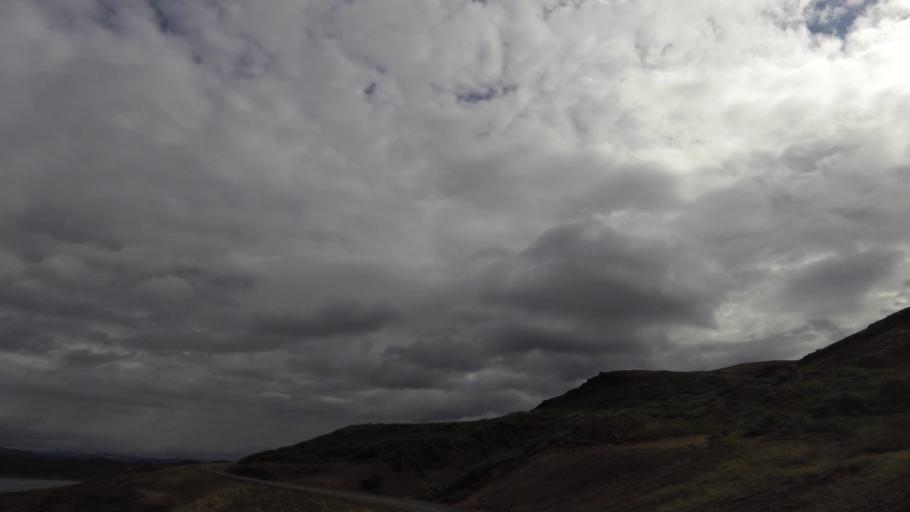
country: IS
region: West
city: Stykkisholmur
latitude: 65.5227
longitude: -22.1213
